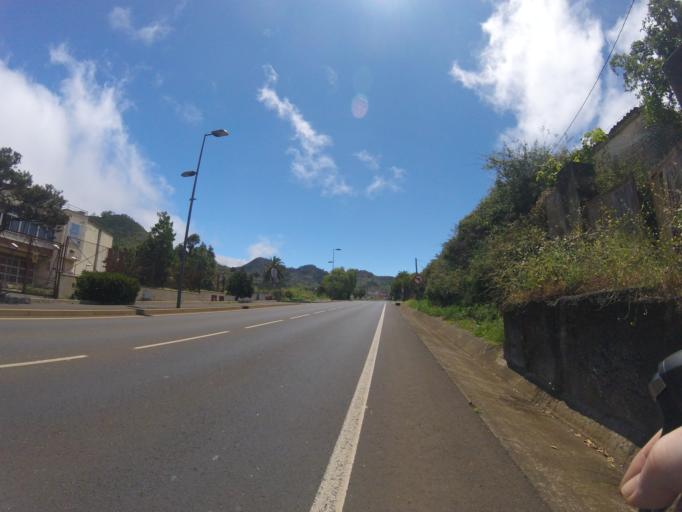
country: ES
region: Canary Islands
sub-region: Provincia de Santa Cruz de Tenerife
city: Tegueste
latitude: 28.5193
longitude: -16.3288
